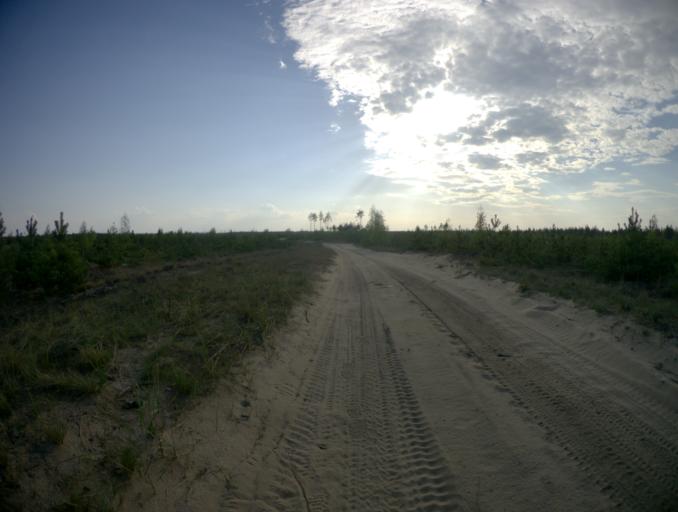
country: RU
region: Vladimir
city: Vyazniki
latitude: 56.4065
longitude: 42.1920
